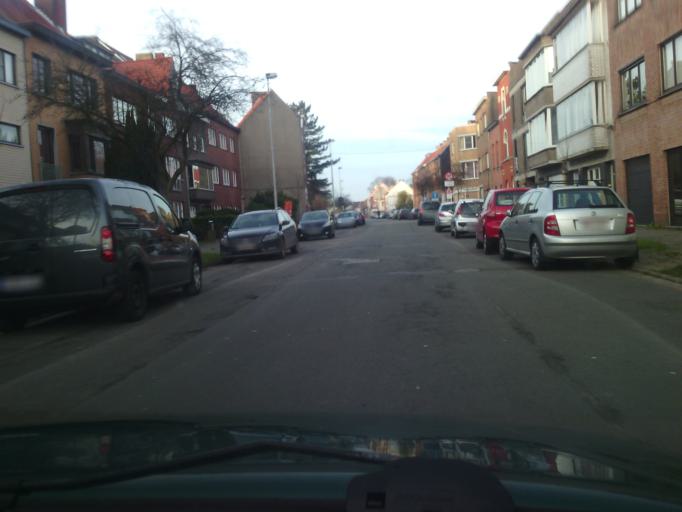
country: BE
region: Flanders
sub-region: Provincie Oost-Vlaanderen
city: Gent
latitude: 51.0601
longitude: 3.6921
